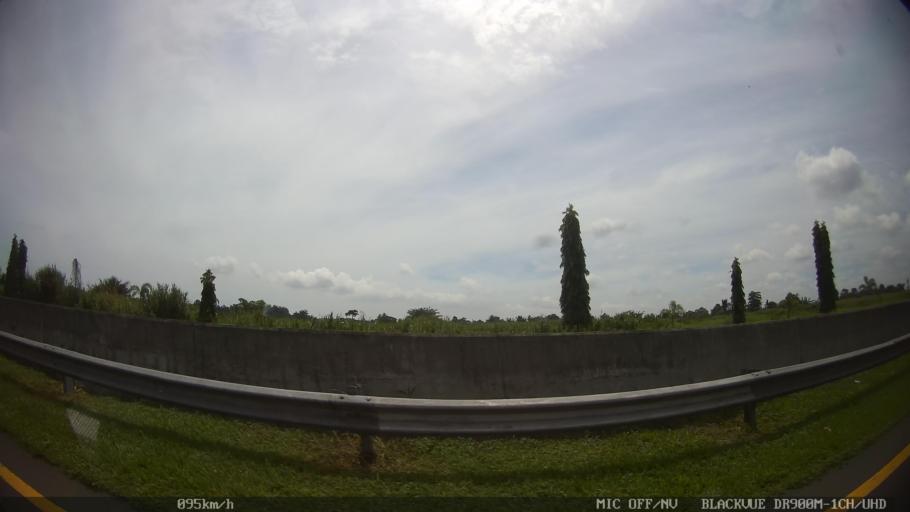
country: ID
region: North Sumatra
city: Labuhan Deli
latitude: 3.7129
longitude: 98.6822
